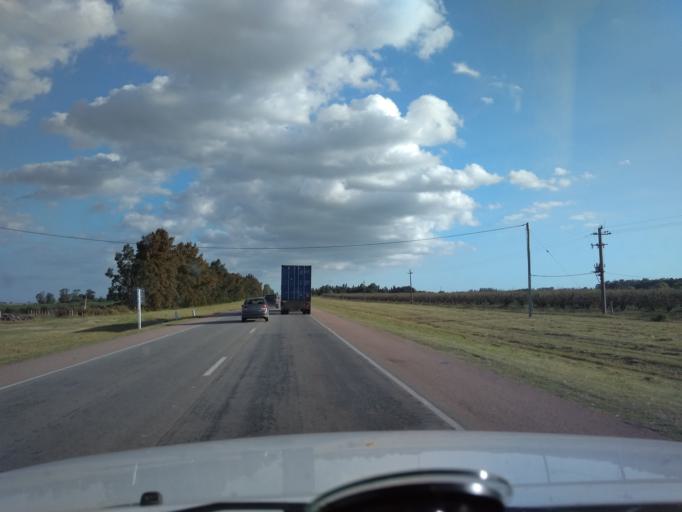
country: UY
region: Canelones
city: Canelones
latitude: -34.3972
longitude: -56.2563
